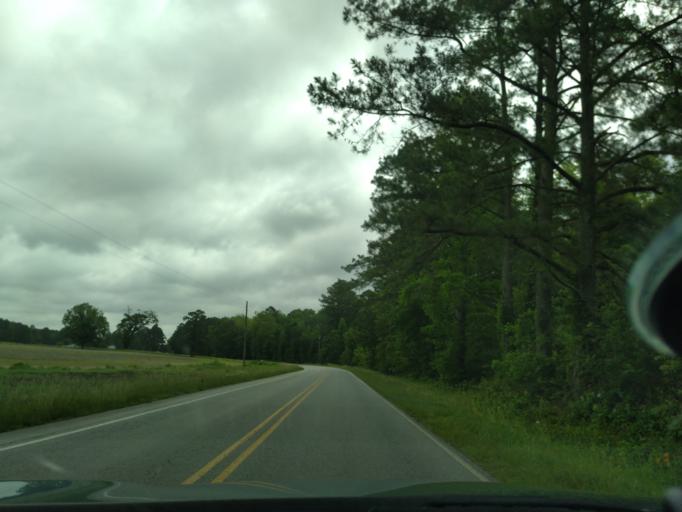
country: US
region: North Carolina
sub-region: Washington County
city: Plymouth
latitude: 35.8579
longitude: -76.7140
